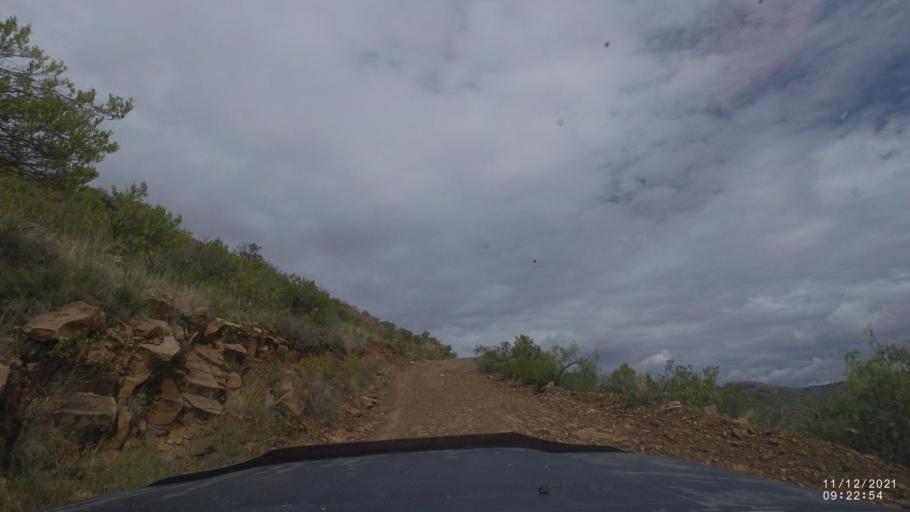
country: BO
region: Cochabamba
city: Tarata
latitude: -17.8776
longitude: -65.9769
